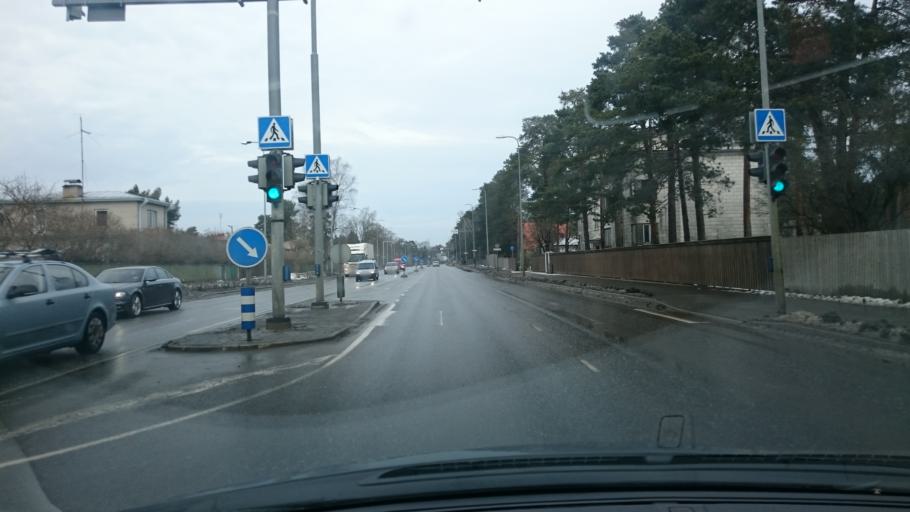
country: EE
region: Harju
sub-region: Tallinna linn
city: Tallinn
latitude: 59.3825
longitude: 24.7176
